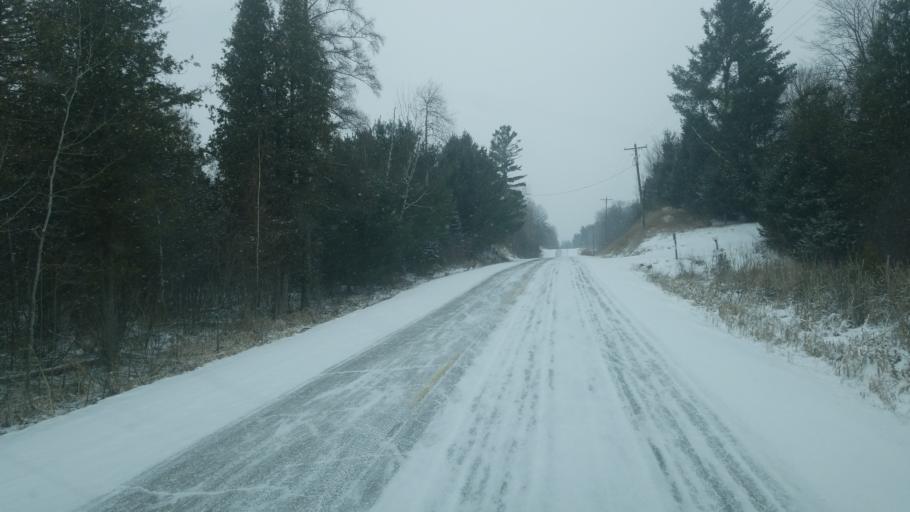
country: US
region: Michigan
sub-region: Osceola County
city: Reed City
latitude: 43.8006
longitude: -85.4025
